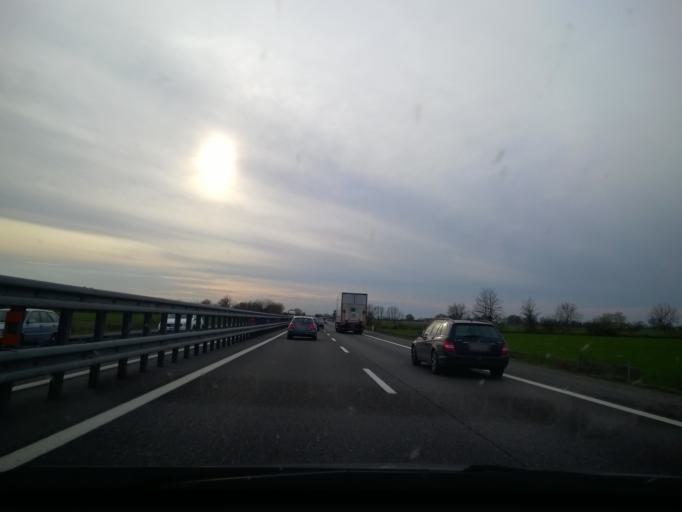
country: IT
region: Emilia-Romagna
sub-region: Provincia di Piacenza
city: San Nicolo
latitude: 45.0643
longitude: 9.5846
